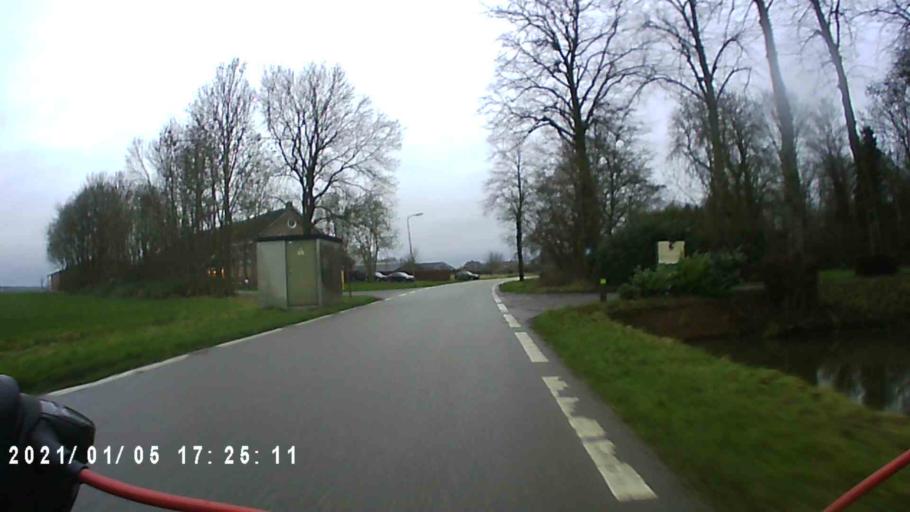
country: NL
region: Groningen
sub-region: Gemeente Delfzijl
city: Delfzijl
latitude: 53.2298
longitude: 6.9620
